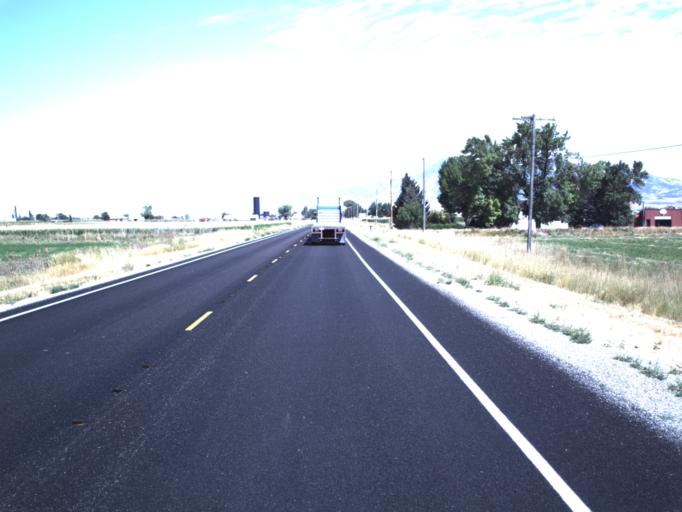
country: US
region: Utah
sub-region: Box Elder County
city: Garland
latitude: 41.7619
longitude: -112.1486
